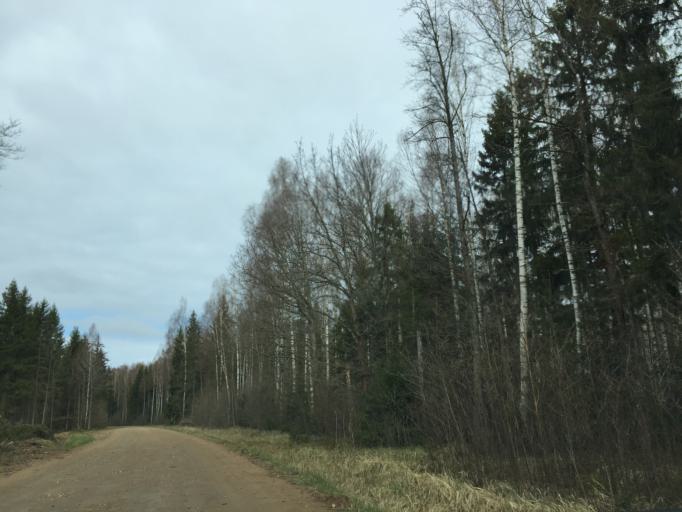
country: LV
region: Saulkrastu
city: Saulkrasti
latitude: 57.5053
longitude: 24.4196
